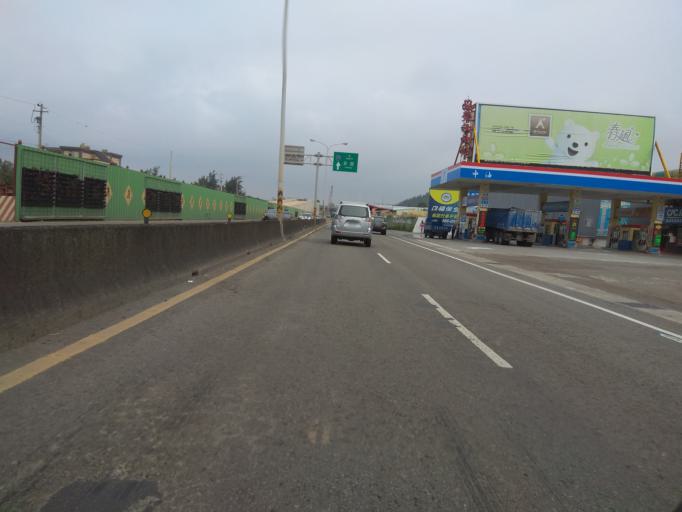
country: TW
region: Taiwan
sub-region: Hsinchu
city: Zhubei
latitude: 24.8725
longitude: 120.9539
